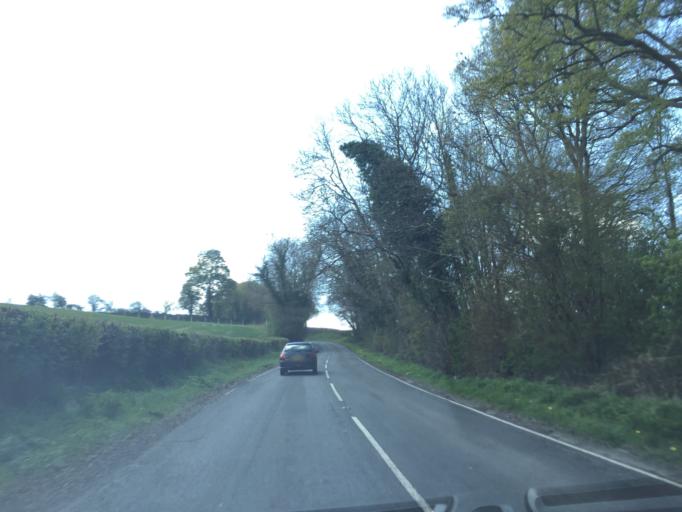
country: GB
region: England
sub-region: Kent
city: Edenbridge
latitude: 51.1414
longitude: 0.1077
